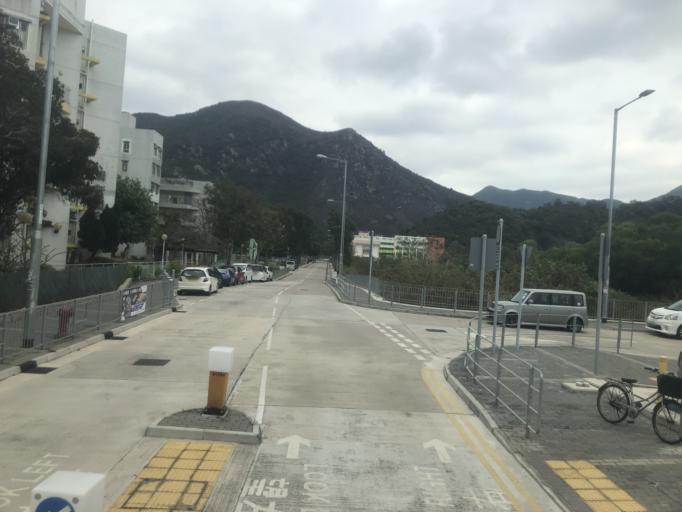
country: HK
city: Tai O
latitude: 22.2527
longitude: 113.8632
